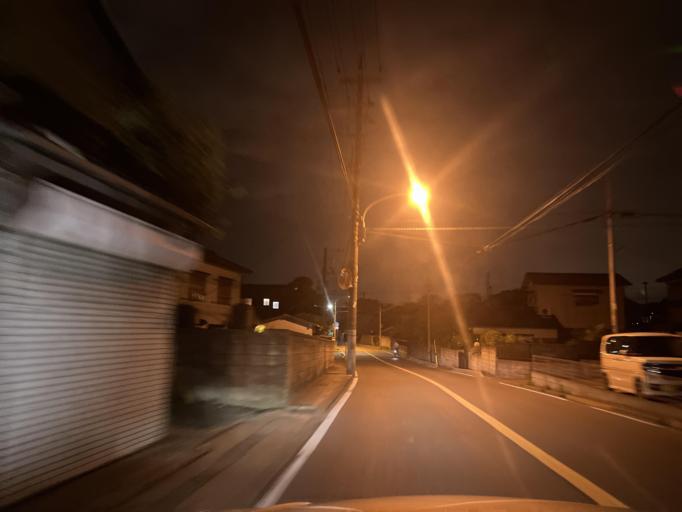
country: JP
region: Chiba
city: Matsudo
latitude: 35.7393
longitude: 139.9355
